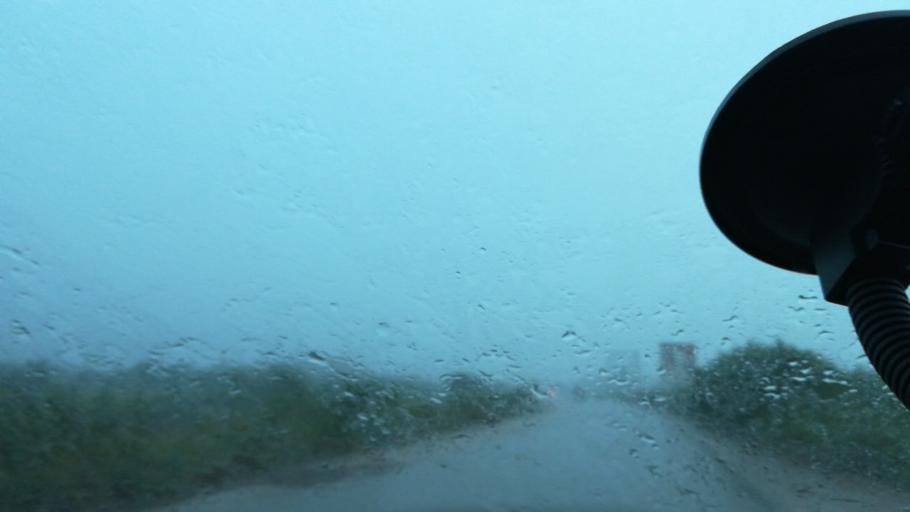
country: CD
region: Katanga
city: Lubumbashi
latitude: -11.5948
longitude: 27.4982
